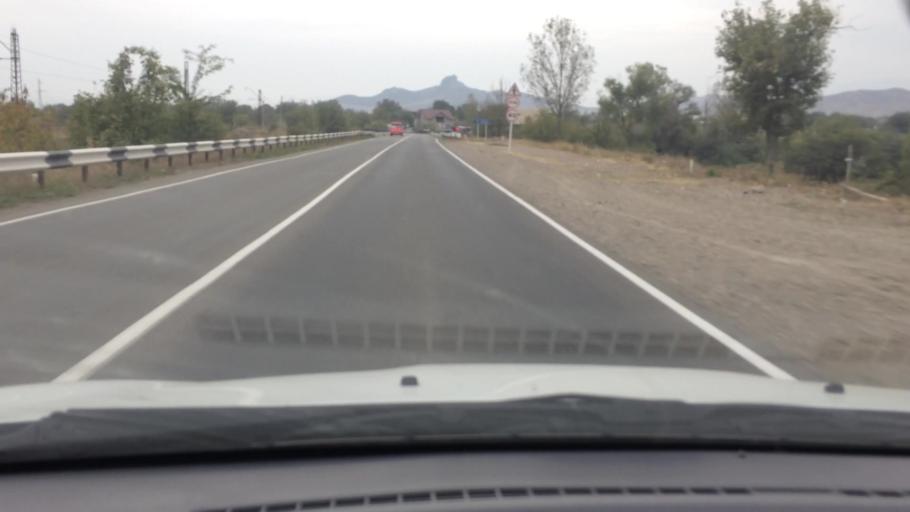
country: GE
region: Kvemo Kartli
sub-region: Marneuli
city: Marneuli
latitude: 41.4062
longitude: 44.8309
